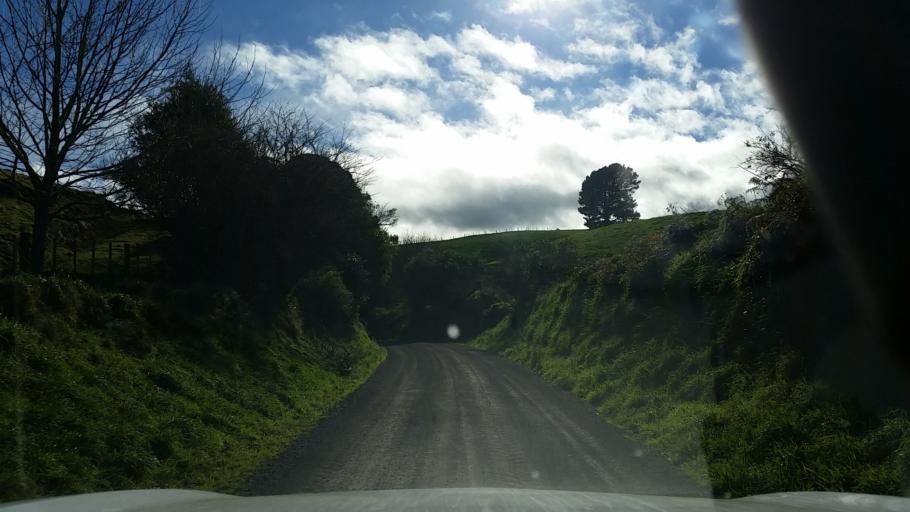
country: NZ
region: Waikato
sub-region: Taupo District
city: Taupo
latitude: -38.4336
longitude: 176.1587
